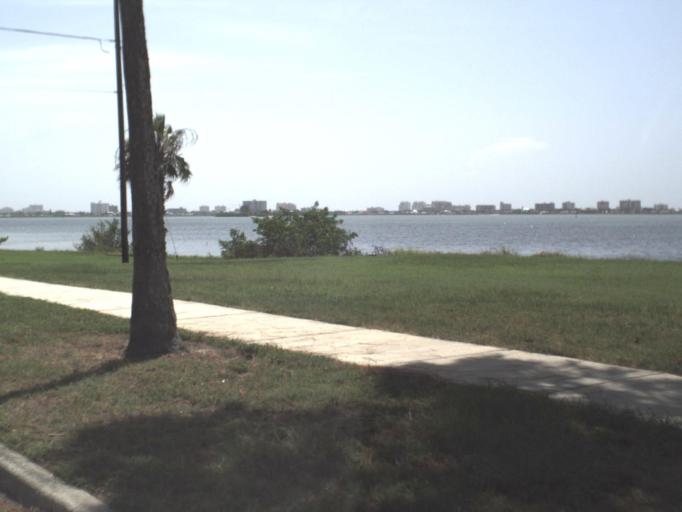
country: US
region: Florida
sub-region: Pinellas County
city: Dunedin
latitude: 28.0005
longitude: -82.7934
